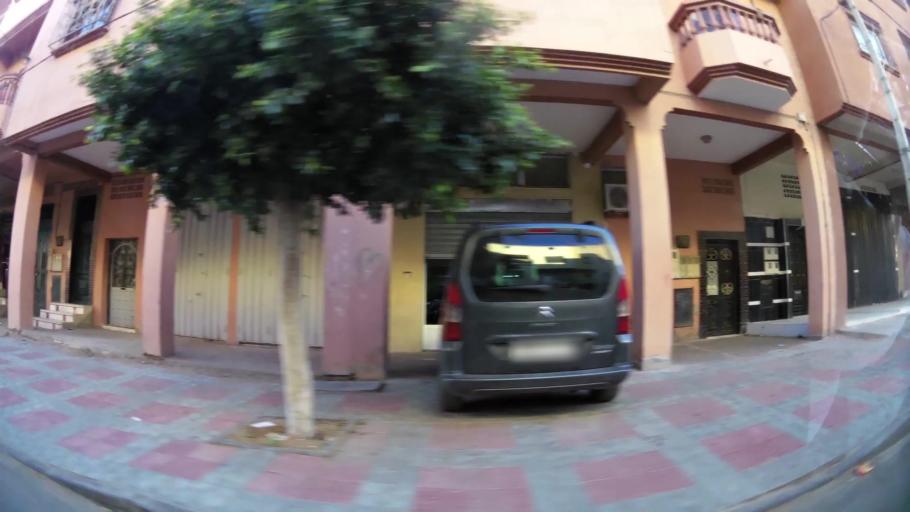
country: MA
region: Marrakech-Tensift-Al Haouz
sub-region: Kelaa-Des-Sraghna
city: Sidi Abdallah
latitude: 32.2391
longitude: -7.9626
